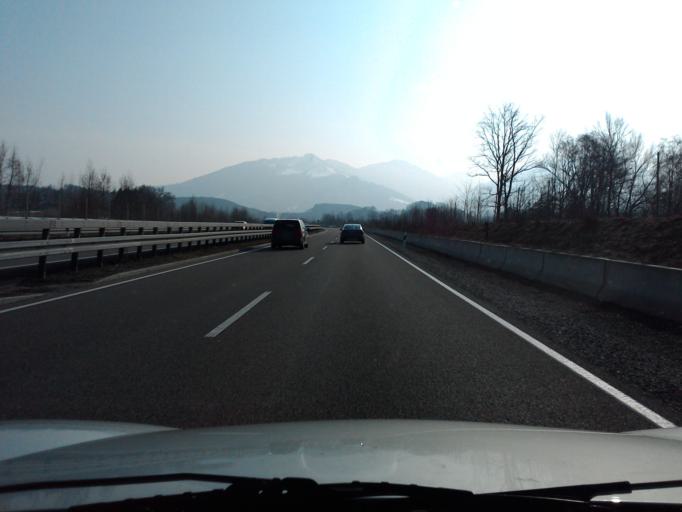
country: DE
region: Bavaria
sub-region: Swabia
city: Immenstadt im Allgau
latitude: 47.5830
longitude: 10.2524
